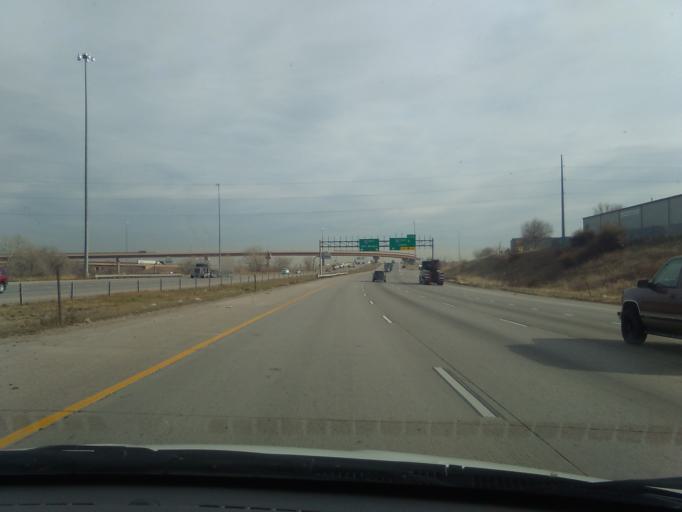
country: US
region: Colorado
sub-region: Adams County
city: Welby
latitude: 39.8223
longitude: -104.9727
